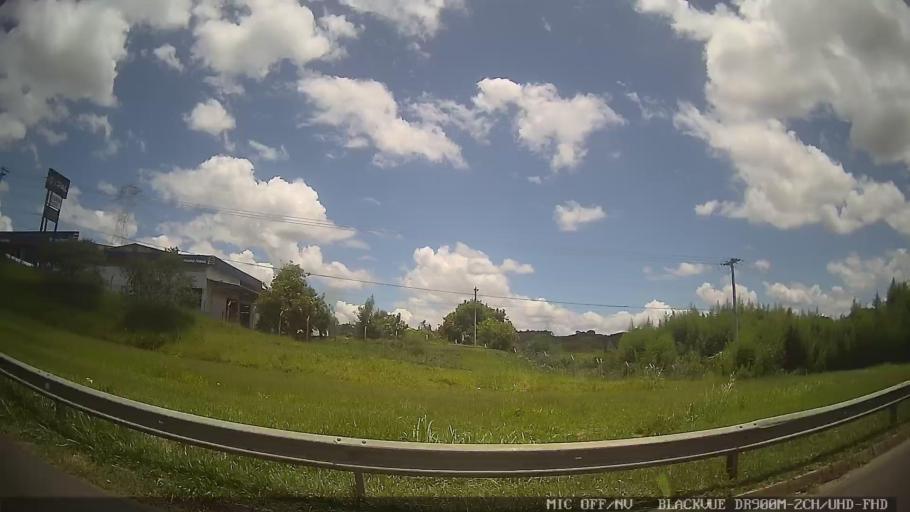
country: BR
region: Sao Paulo
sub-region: Jarinu
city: Jarinu
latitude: -23.0513
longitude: -46.6659
